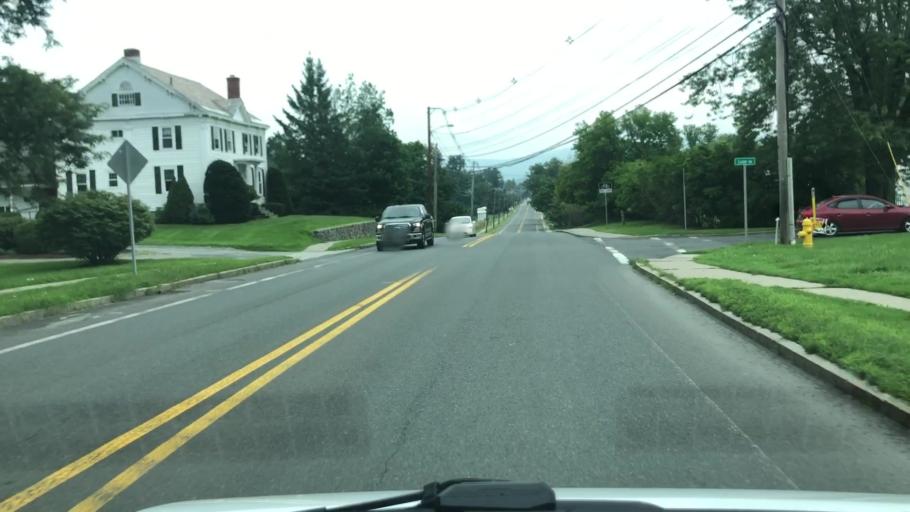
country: US
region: Massachusetts
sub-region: Berkshire County
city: Williamstown
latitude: 42.7016
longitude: -73.1822
